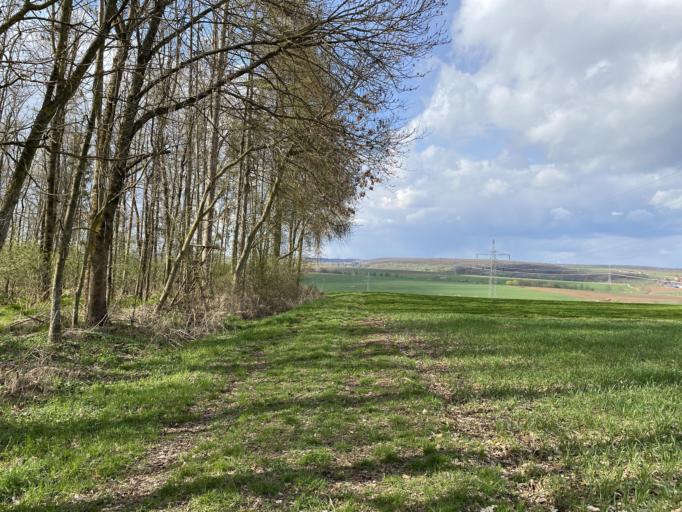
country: DE
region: Bavaria
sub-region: Regierungsbezirk Unterfranken
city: Werneck
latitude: 49.9623
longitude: 10.0663
